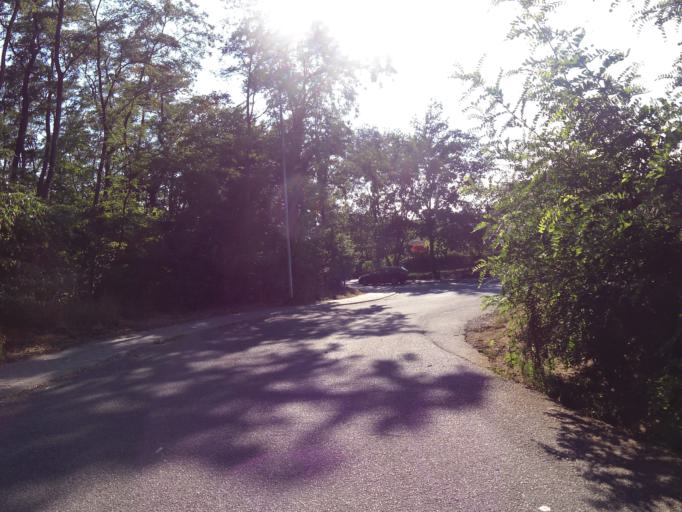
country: DE
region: Hesse
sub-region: Regierungsbezirk Darmstadt
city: Nauheim
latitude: 49.9678
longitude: 8.4552
